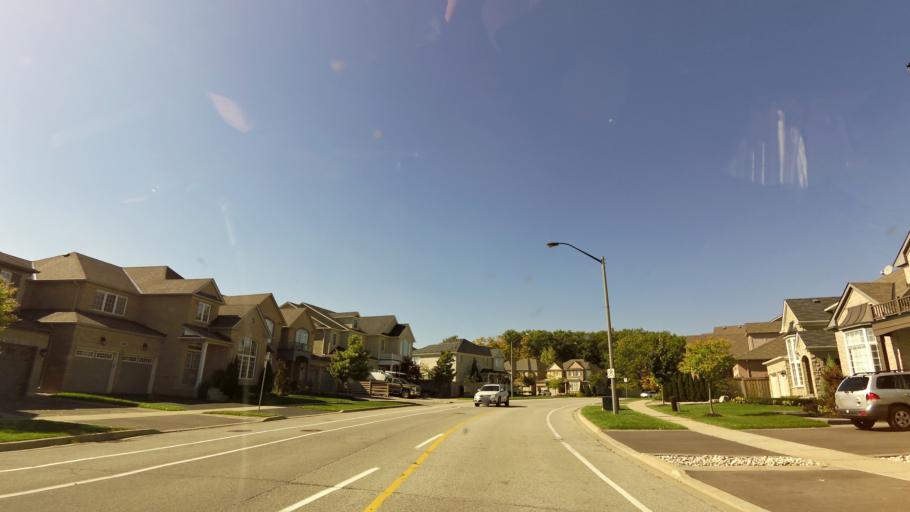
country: CA
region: Ontario
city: Burlington
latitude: 43.4235
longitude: -79.7732
